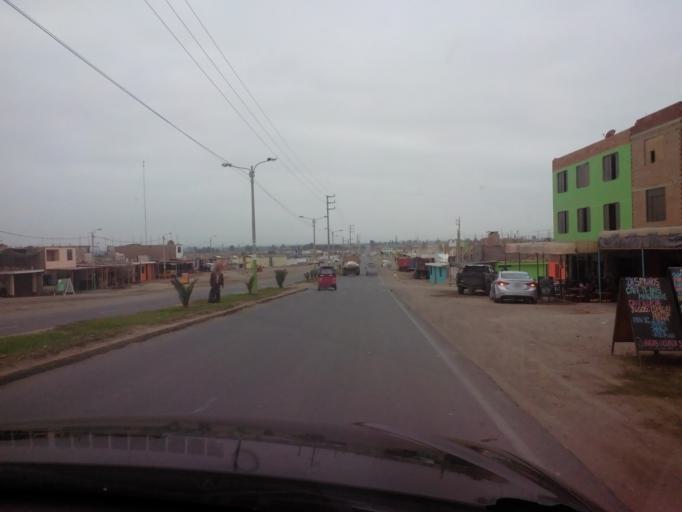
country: PE
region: Ica
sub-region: Provincia de Pisco
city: San Clemente
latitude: -13.6805
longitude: -76.1518
